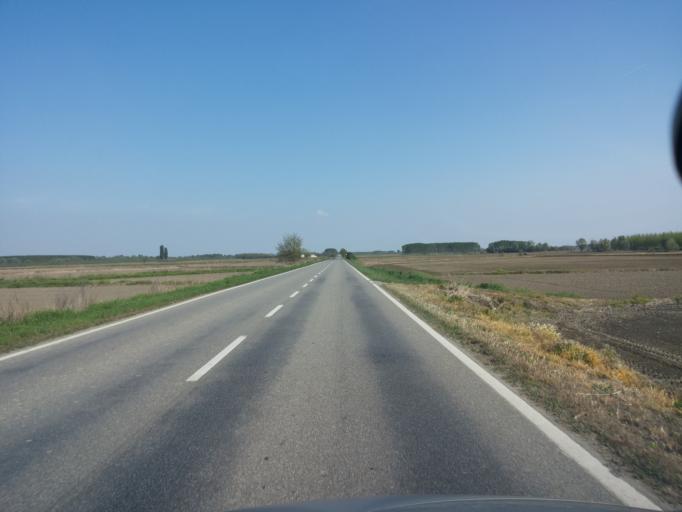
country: IT
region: Piedmont
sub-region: Provincia di Vercelli
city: Caresana
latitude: 45.2125
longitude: 8.5158
